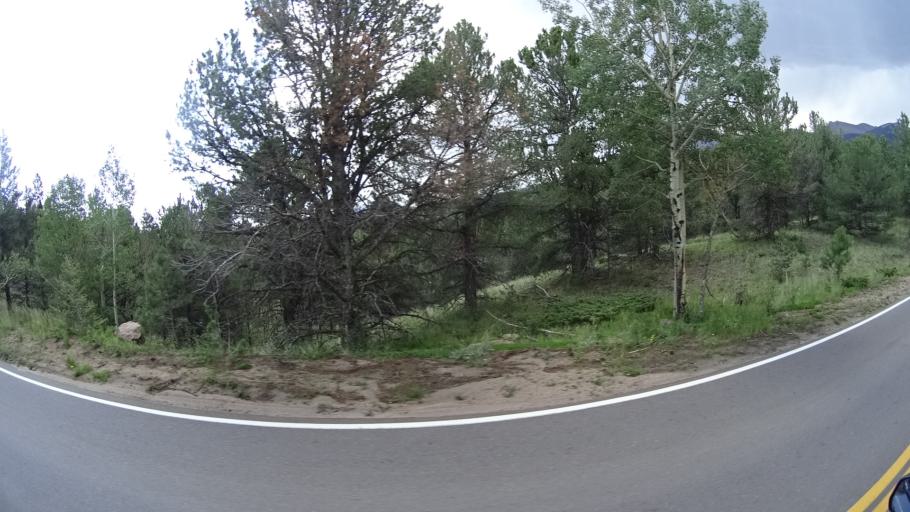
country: US
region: Colorado
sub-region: El Paso County
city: Cascade-Chipita Park
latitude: 38.9145
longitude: -105.0280
